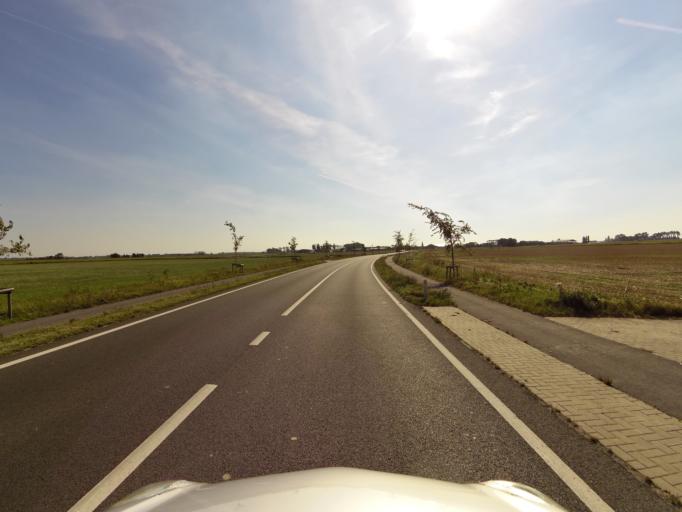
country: BE
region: Flanders
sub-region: Provincie West-Vlaanderen
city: Gistel
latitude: 51.1154
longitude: 2.8909
